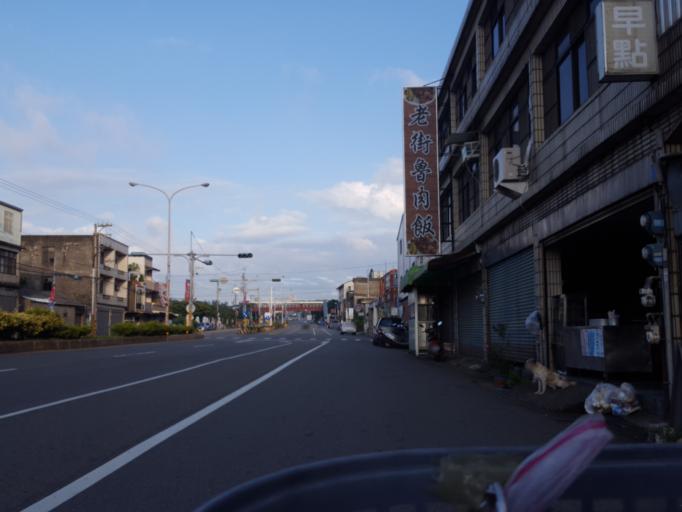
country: TW
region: Taiwan
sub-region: Hsinchu
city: Zhubei
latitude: 24.8783
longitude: 121.0578
